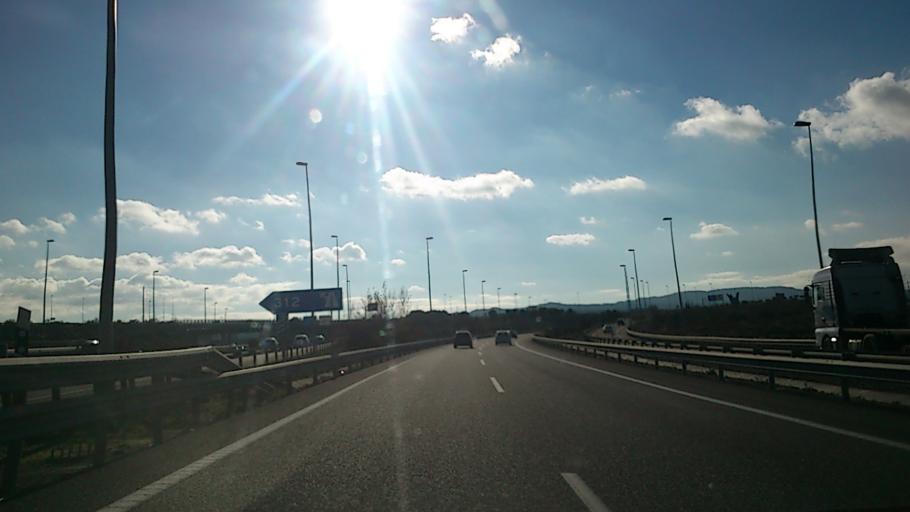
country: ES
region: Aragon
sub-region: Provincia de Zaragoza
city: Montecanal
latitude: 41.6385
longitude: -0.9734
